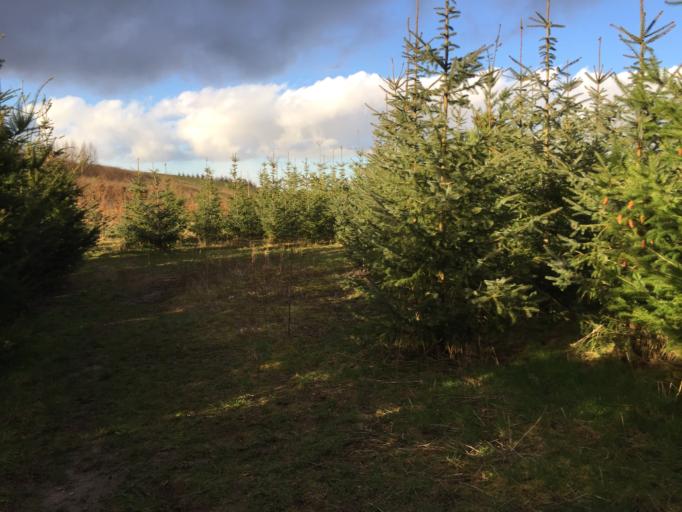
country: DK
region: South Denmark
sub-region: Odense Kommune
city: Bellinge
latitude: 55.3722
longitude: 10.3126
